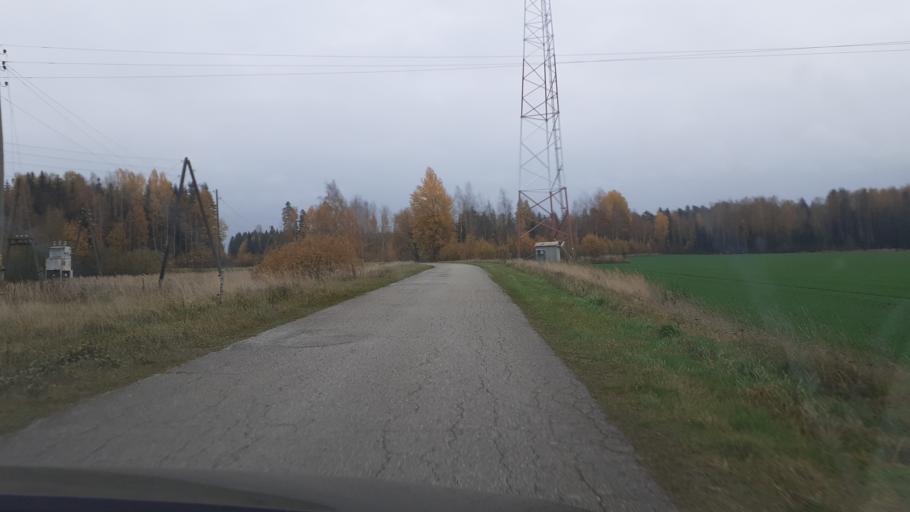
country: LV
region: Skrunda
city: Skrunda
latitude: 56.8562
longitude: 22.2386
